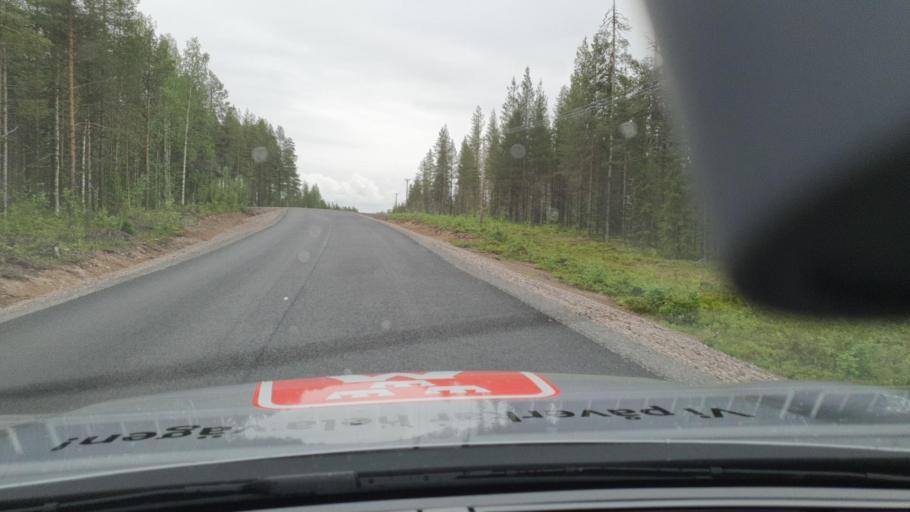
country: SE
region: Norrbotten
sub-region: Overtornea Kommun
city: OEvertornea
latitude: 66.6512
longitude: 23.2336
